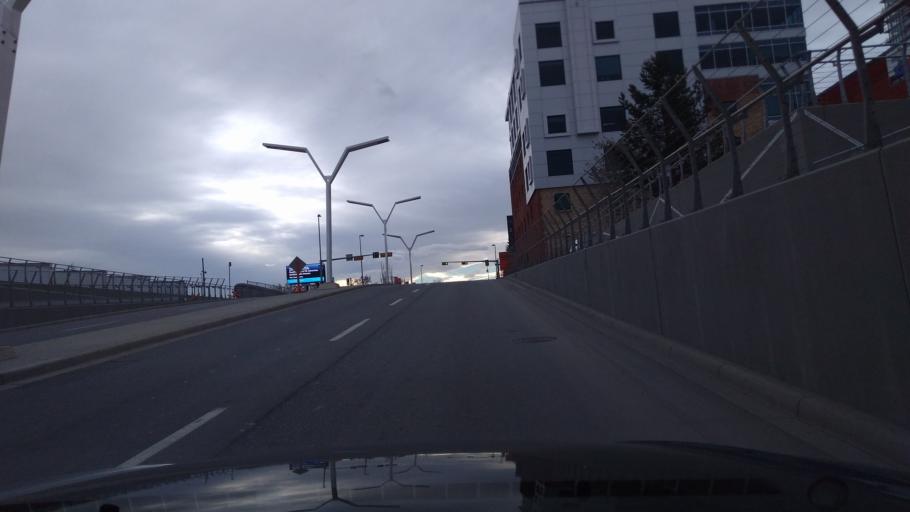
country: CA
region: Alberta
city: Calgary
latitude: 51.0432
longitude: -114.0535
